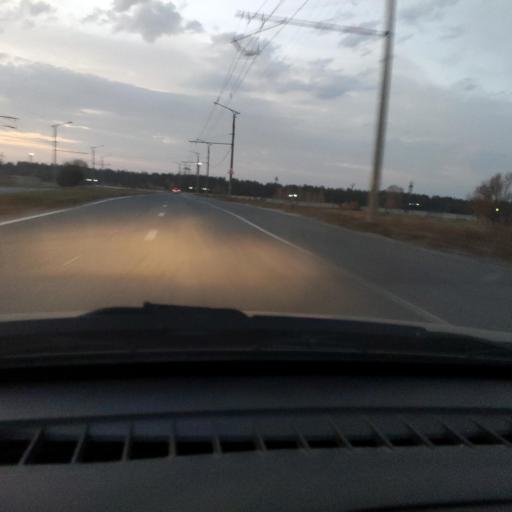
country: RU
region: Samara
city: Povolzhskiy
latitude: 53.5461
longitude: 49.6032
